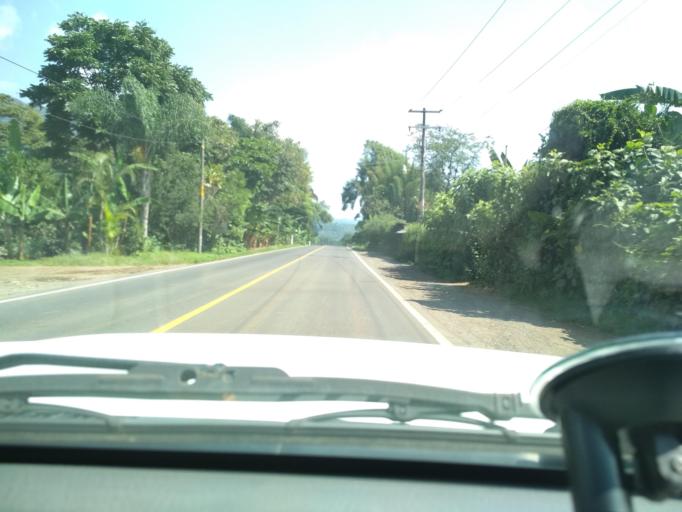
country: MX
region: Veracruz
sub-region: Fortin
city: Santa Lucia Potrerillo
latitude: 18.9768
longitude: -97.0164
